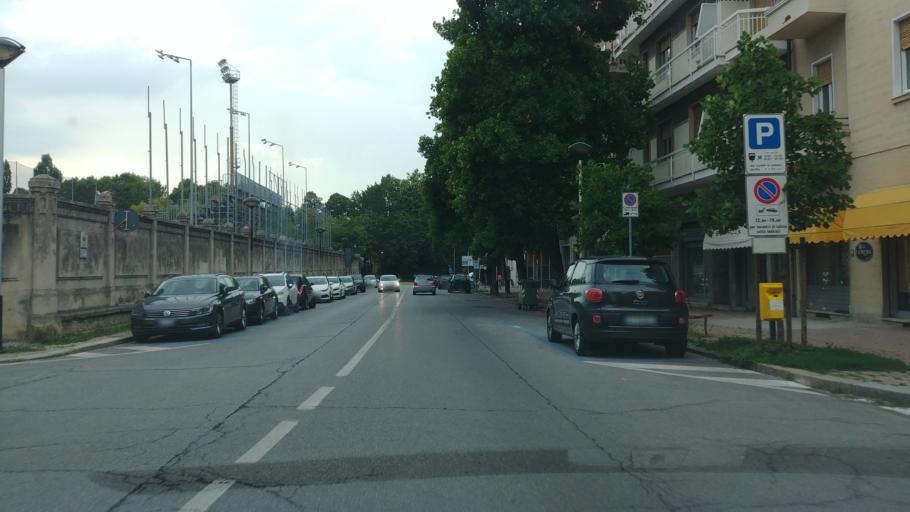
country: IT
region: Piedmont
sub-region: Provincia di Cuneo
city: Cuneo
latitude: 44.3834
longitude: 7.5354
